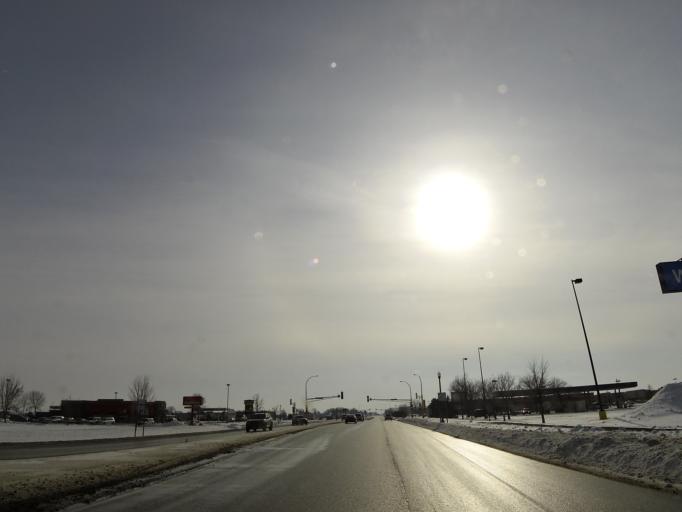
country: US
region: Minnesota
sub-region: McLeod County
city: Hutchinson
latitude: 44.8722
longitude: -94.3757
